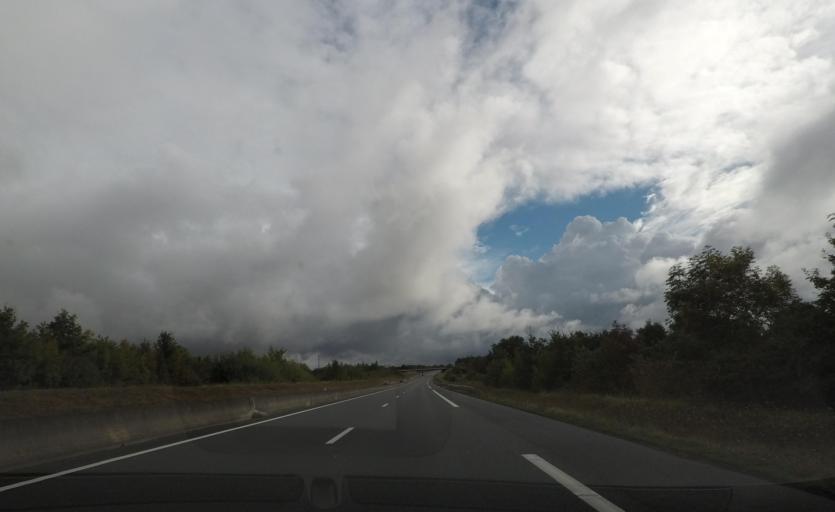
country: FR
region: Pays de la Loire
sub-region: Departement de la Vendee
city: La Roche-sur-Yon
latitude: 46.6499
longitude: -1.3879
